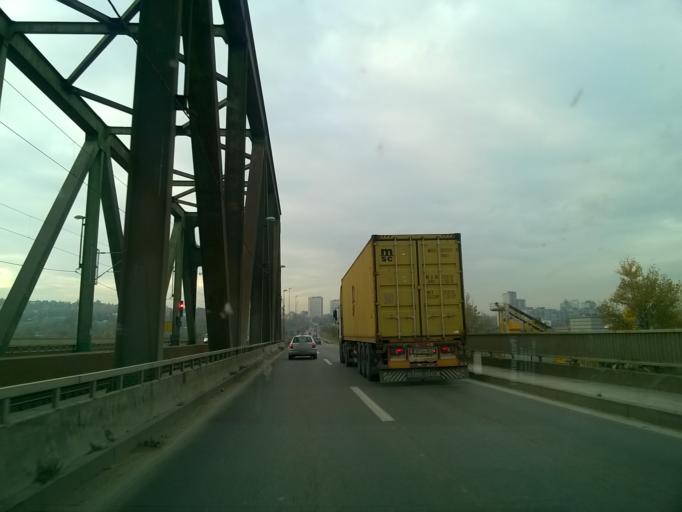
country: RS
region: Central Serbia
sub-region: Belgrade
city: Palilula
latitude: 44.8252
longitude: 20.4912
